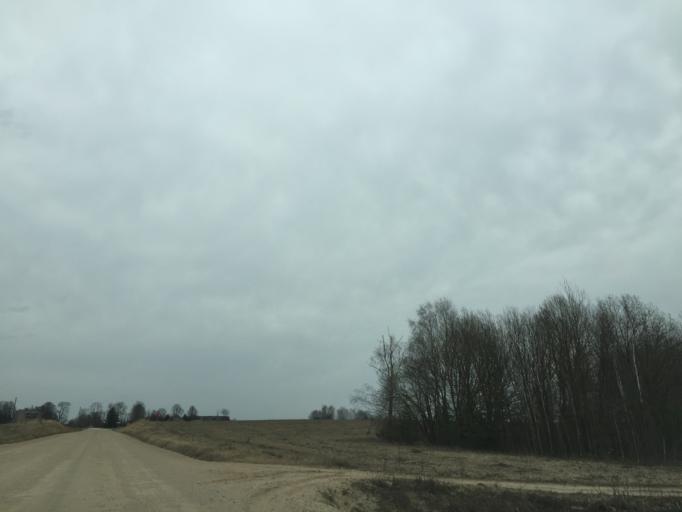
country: LV
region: Livani
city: Livani
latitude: 56.3263
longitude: 26.1585
